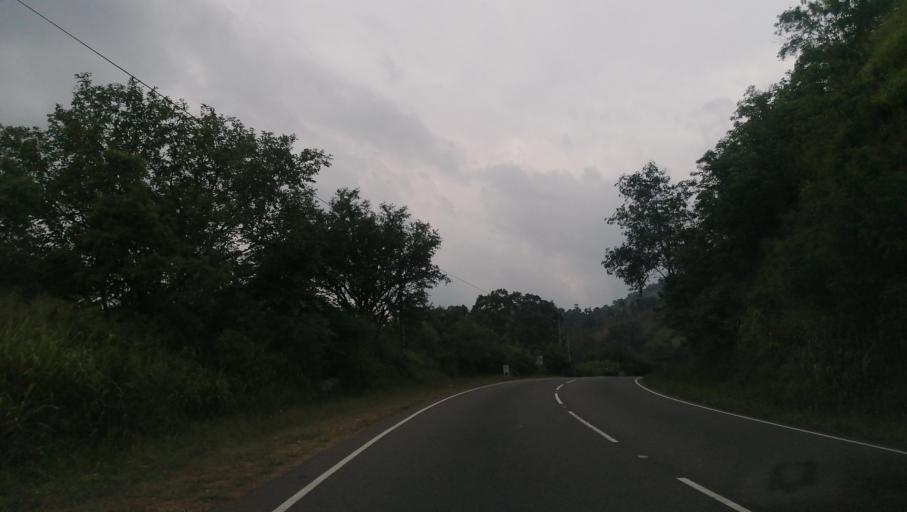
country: LK
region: Central
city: Kandy
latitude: 7.2410
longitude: 80.7260
